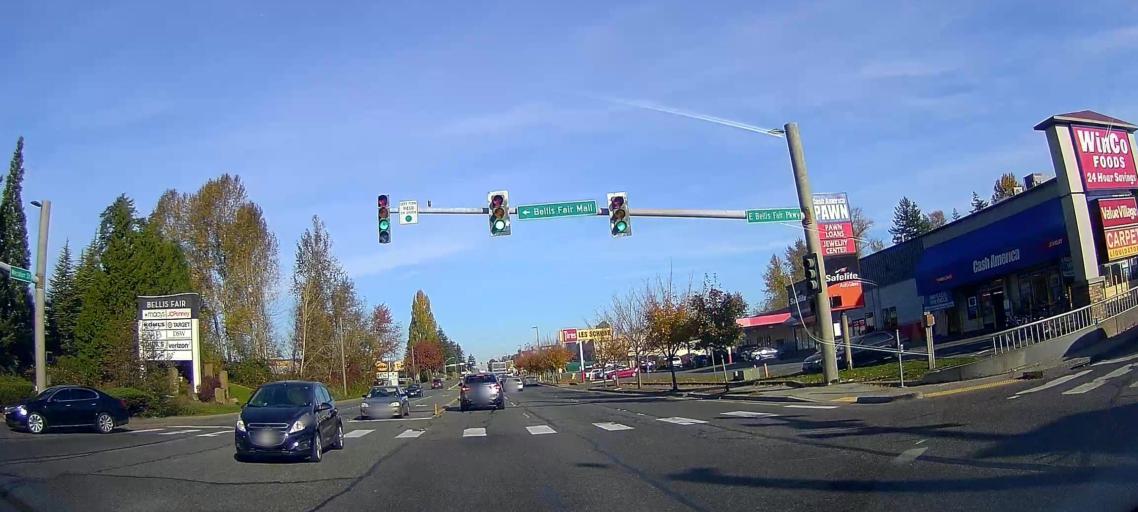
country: US
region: Washington
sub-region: Whatcom County
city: Bellingham
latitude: 48.7873
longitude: -122.4855
